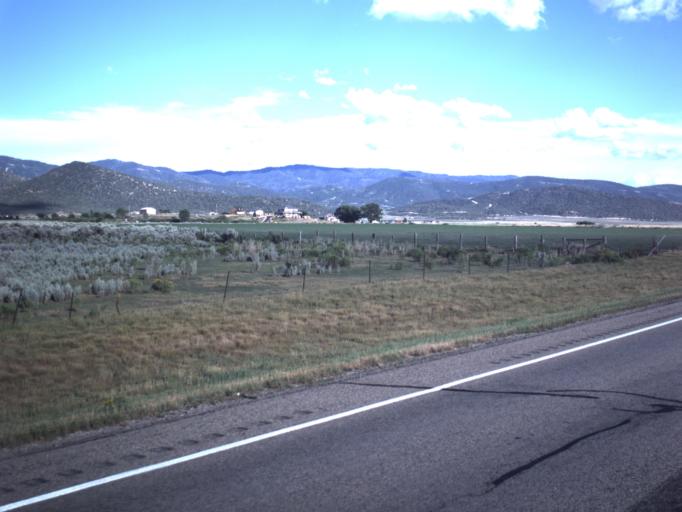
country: US
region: Utah
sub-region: Sanpete County
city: Fairview
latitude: 39.8081
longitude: -111.5045
